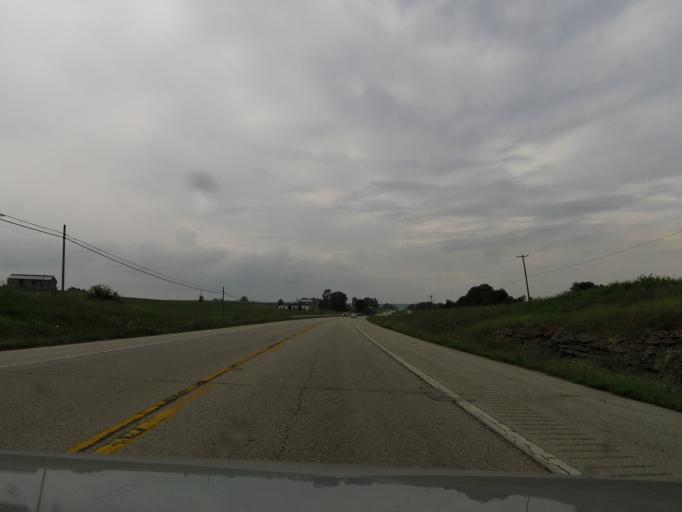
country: US
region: Kentucky
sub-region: Mason County
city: Maysville
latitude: 38.5462
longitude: -83.8238
